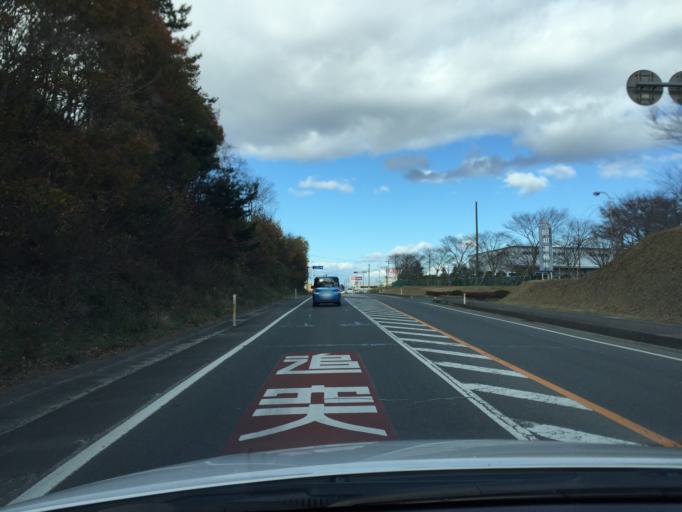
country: JP
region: Fukushima
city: Namie
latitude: 37.6115
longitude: 141.0053
